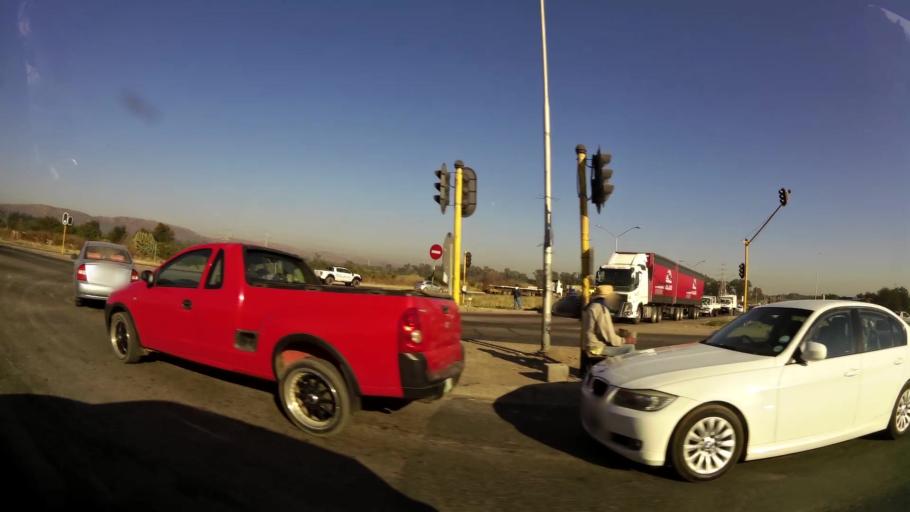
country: ZA
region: Gauteng
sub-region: City of Tshwane Metropolitan Municipality
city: Pretoria
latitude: -25.6610
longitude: 28.1916
